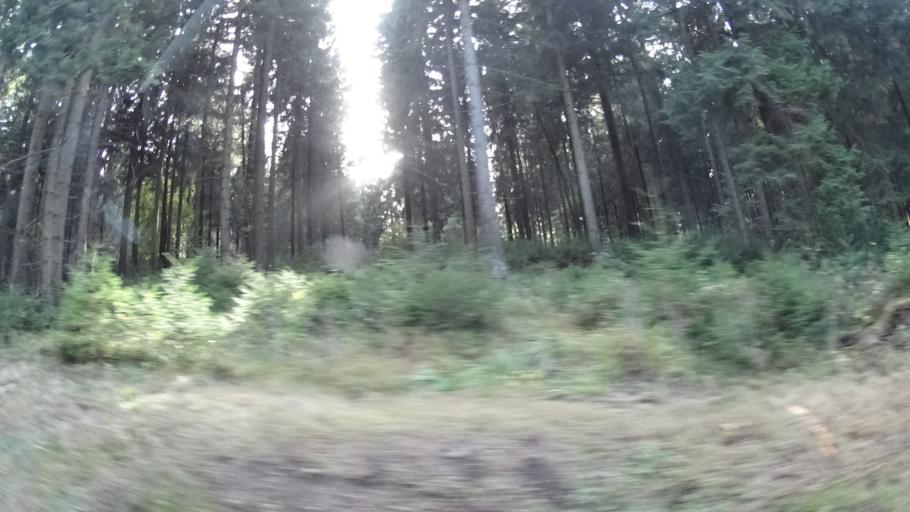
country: DE
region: Thuringia
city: Bermbach
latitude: 50.6903
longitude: 10.6373
